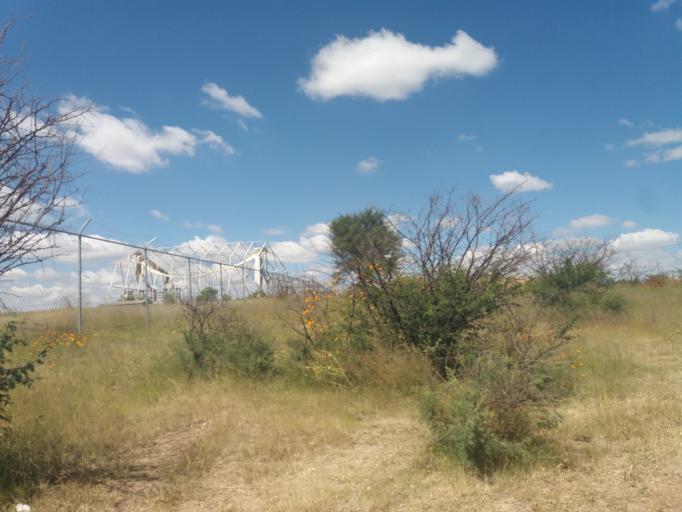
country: MX
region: Aguascalientes
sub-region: Aguascalientes
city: San Sebastian [Fraccionamiento]
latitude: 21.7909
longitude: -102.2714
